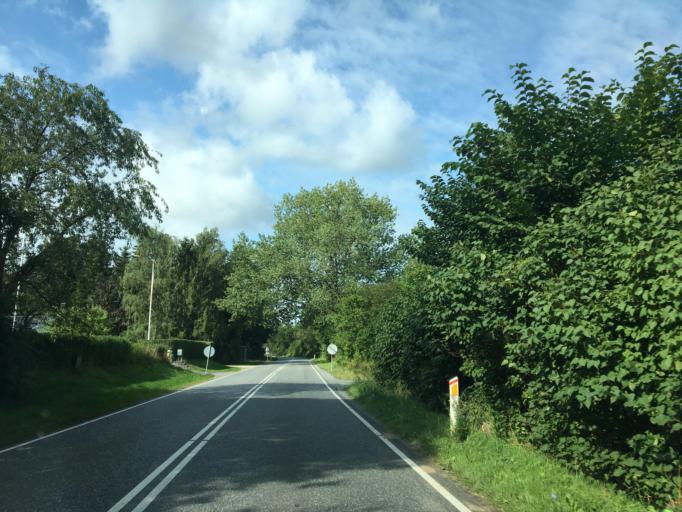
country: DK
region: South Denmark
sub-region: Middelfart Kommune
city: Ejby
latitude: 55.3914
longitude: 9.9360
